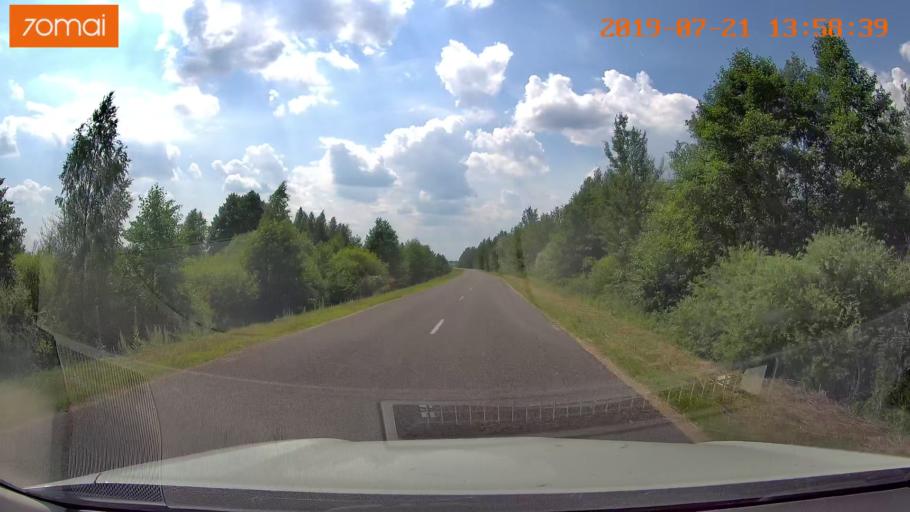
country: BY
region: Grodnenskaya
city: Lyubcha
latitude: 53.7594
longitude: 26.0757
